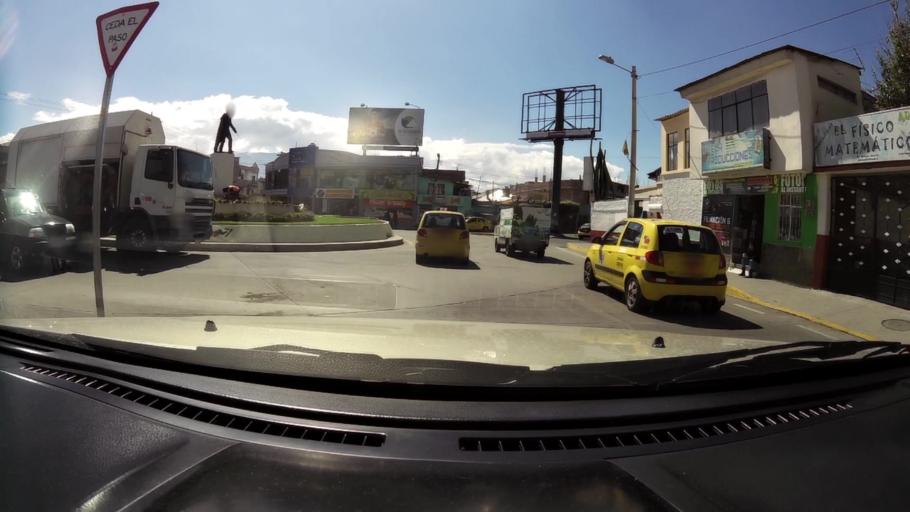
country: EC
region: Chimborazo
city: Riobamba
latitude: -1.6635
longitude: -78.6496
